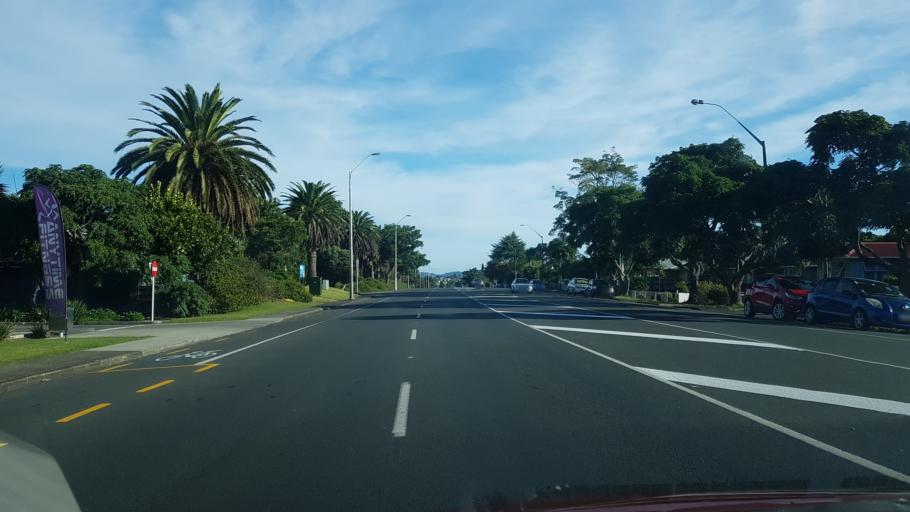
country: NZ
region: Auckland
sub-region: Auckland
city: Rosebank
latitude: -36.8444
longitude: 174.6517
